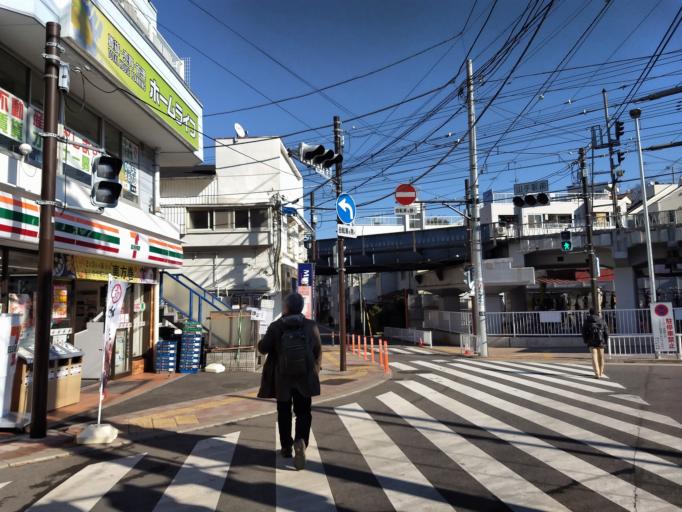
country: JP
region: Kanagawa
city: Yokohama
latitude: 35.4277
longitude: 139.6457
